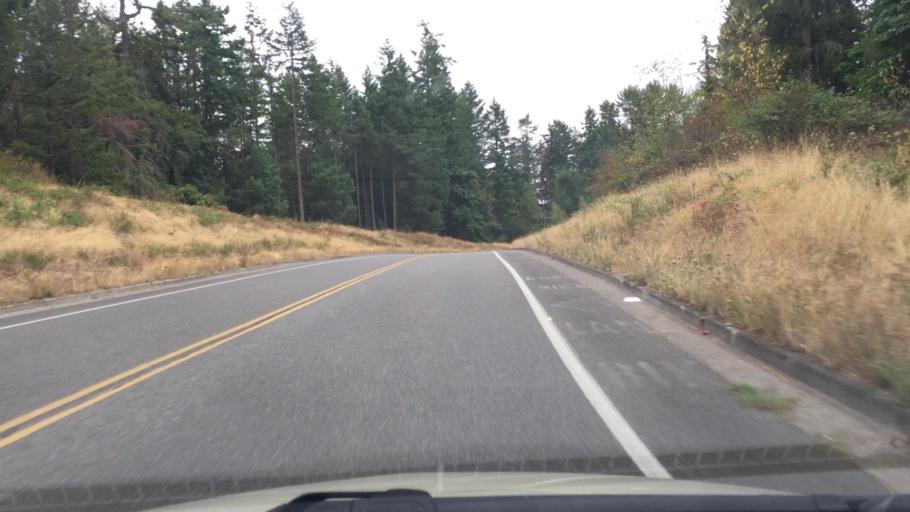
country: US
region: Washington
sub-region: Pierce County
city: Fort Lewis
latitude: 47.1098
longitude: -122.5906
